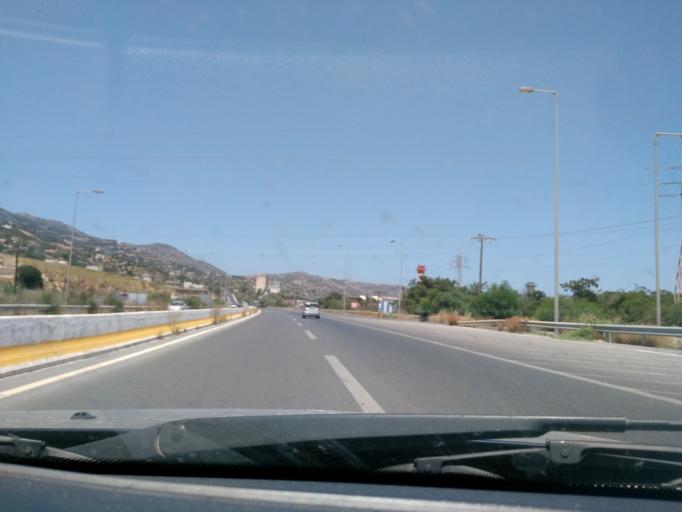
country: GR
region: Crete
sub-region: Nomos Irakleiou
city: Gazi
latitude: 35.3395
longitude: 25.0498
